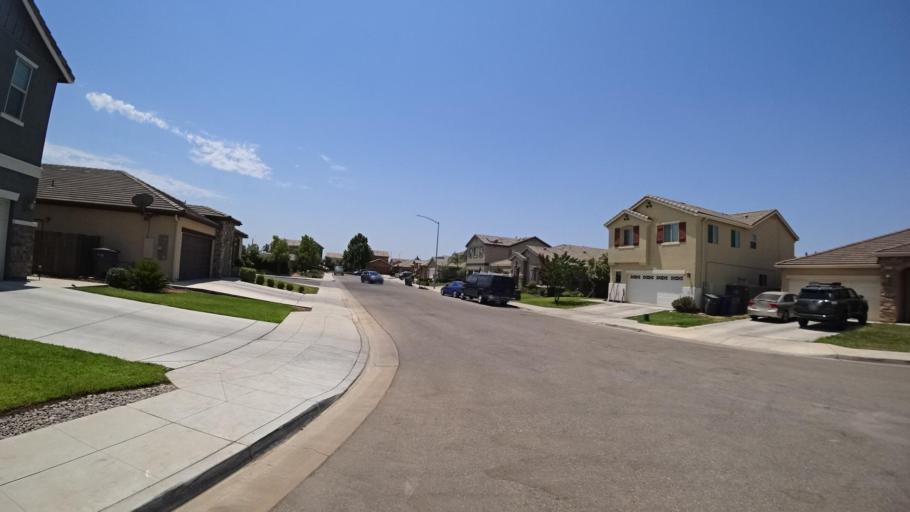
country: US
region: California
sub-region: Fresno County
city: Tarpey Village
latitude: 36.7808
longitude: -119.6556
